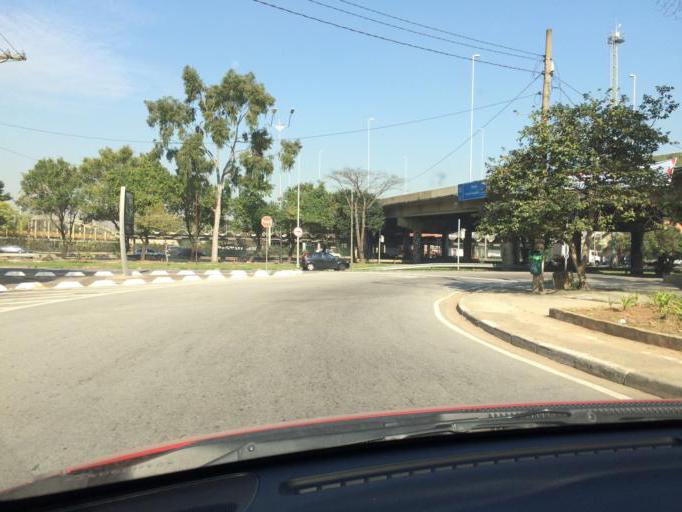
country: BR
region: Sao Paulo
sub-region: Sao Paulo
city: Sao Paulo
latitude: -23.5572
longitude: -46.7105
